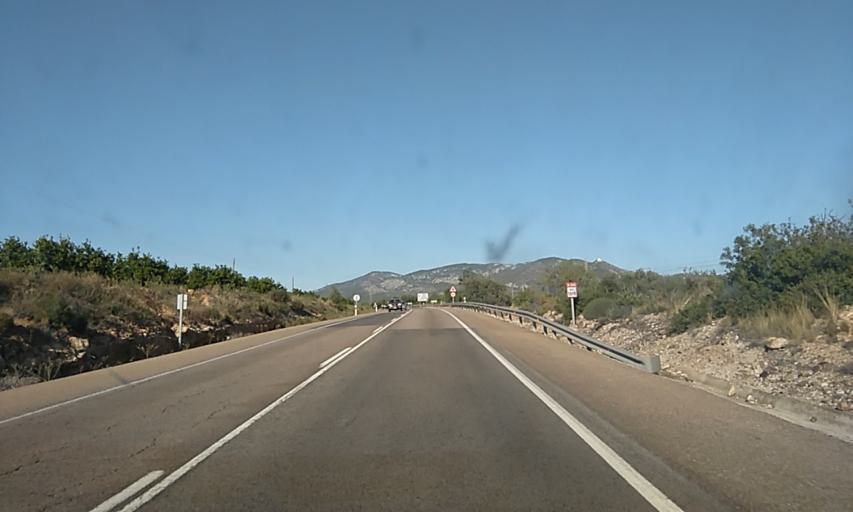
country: ES
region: Valencia
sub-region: Provincia de Castello
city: Torreblanca
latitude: 40.2430
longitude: 0.2299
